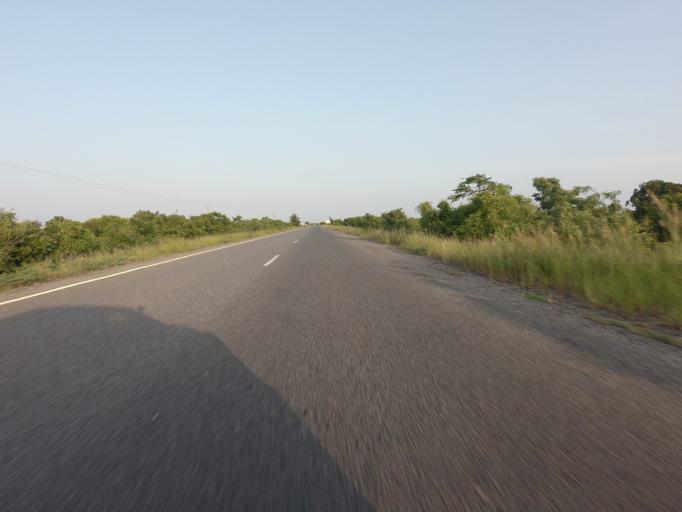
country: GH
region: Volta
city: Anloga
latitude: 5.8836
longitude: 0.7256
